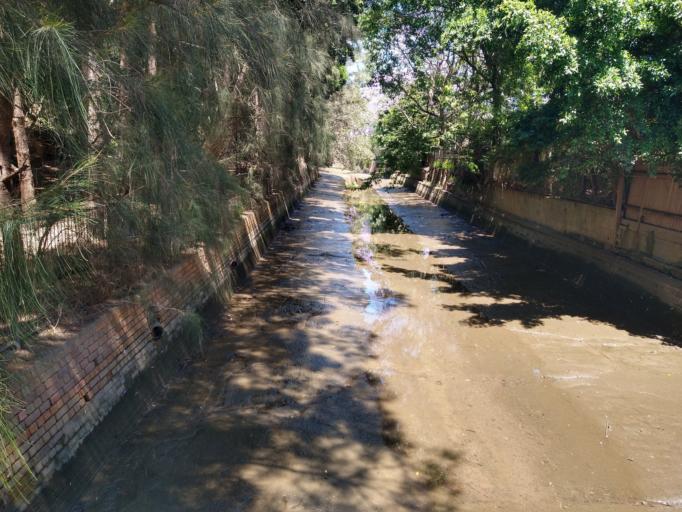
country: AU
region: New South Wales
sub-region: Ashfield
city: Summer Hill
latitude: -33.8863
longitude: 151.1447
